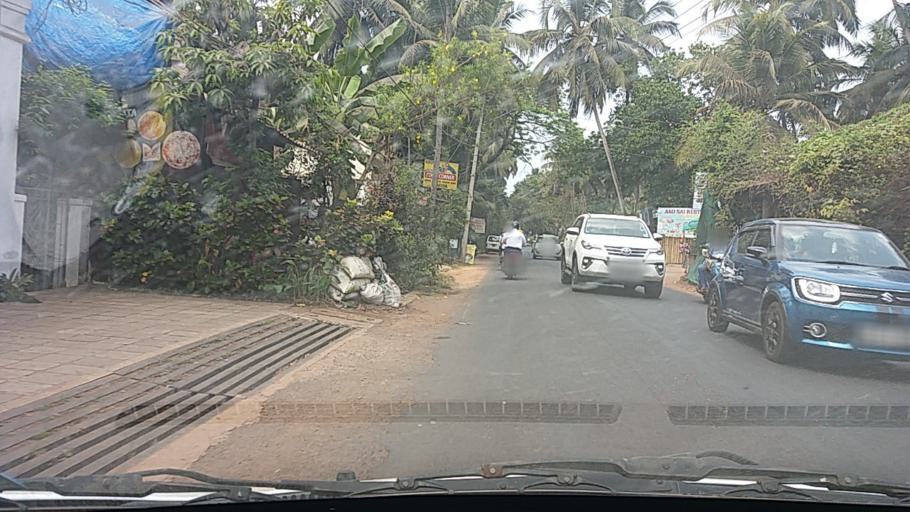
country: IN
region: Goa
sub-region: North Goa
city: Saligao
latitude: 15.5462
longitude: 73.7954
